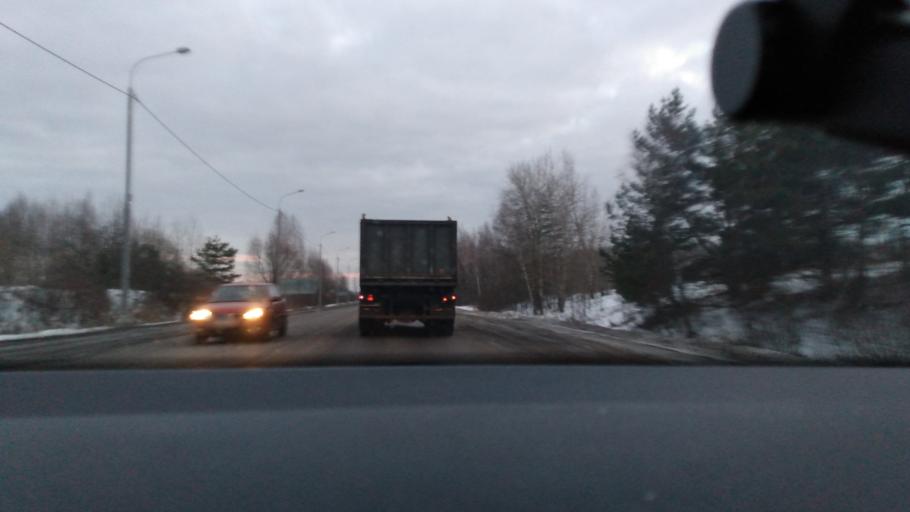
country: RU
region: Moskovskaya
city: Yegor'yevsk
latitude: 55.4135
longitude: 39.0475
